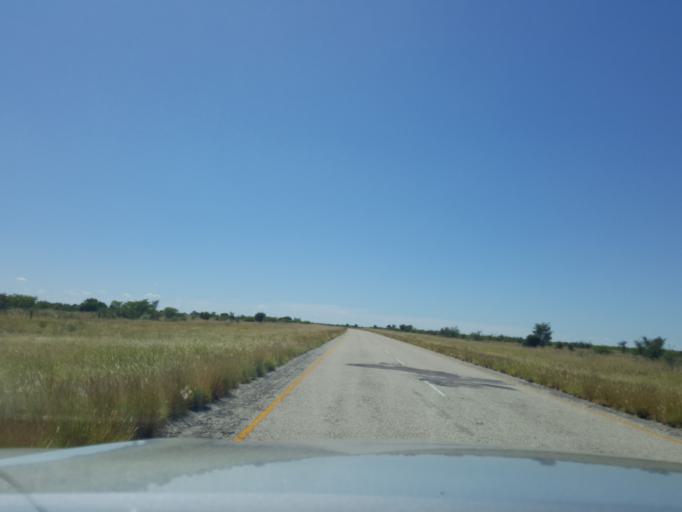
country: BW
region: Central
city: Gweta
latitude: -20.2308
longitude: 24.9687
